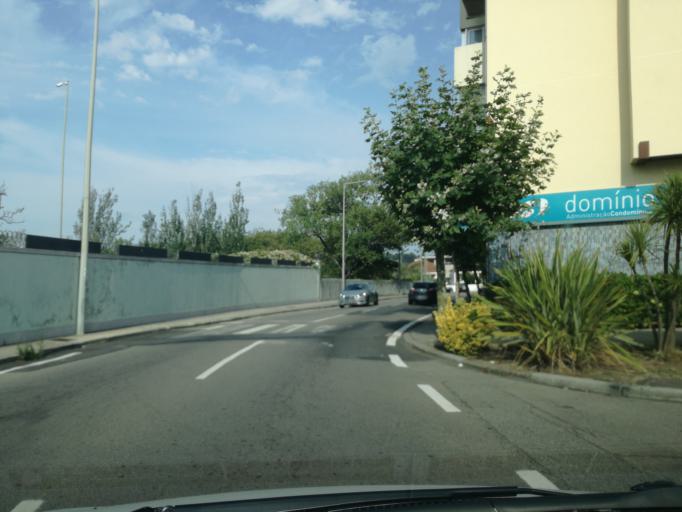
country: PT
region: Aveiro
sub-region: Espinho
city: Espinho
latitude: 41.0121
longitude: -8.6371
